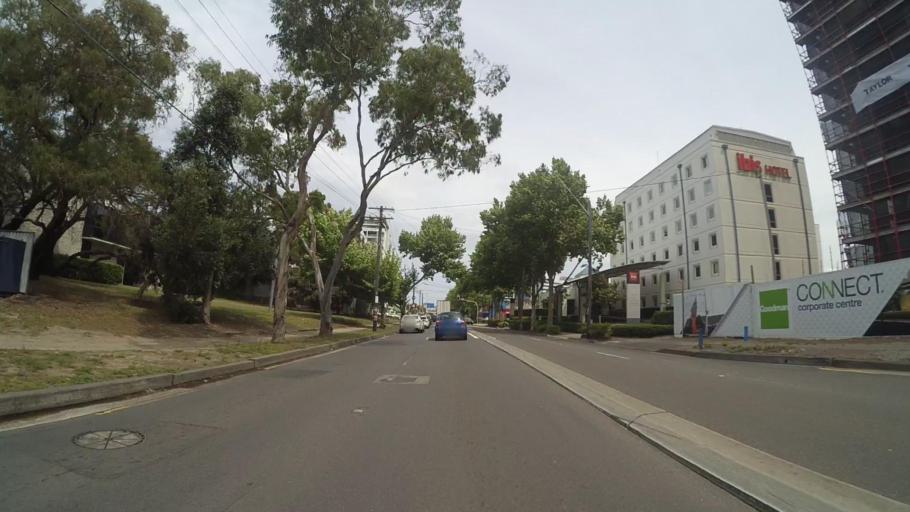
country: AU
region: New South Wales
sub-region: Botany Bay
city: Mascot
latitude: -33.9277
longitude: 151.1874
